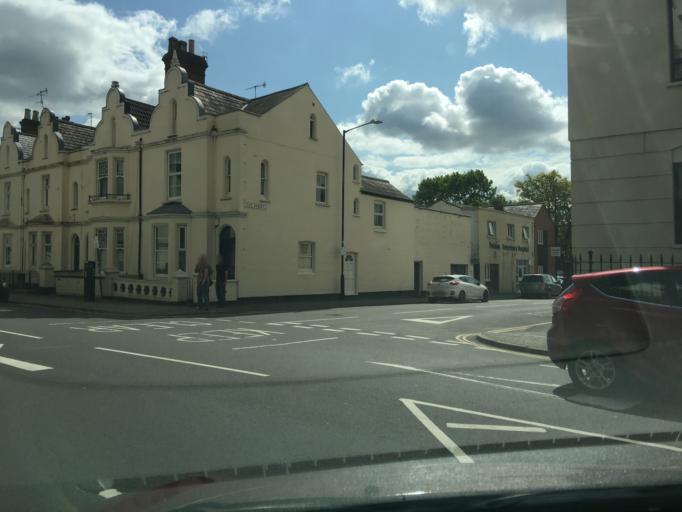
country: GB
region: England
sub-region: Warwickshire
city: Royal Leamington Spa
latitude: 52.2938
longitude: -1.5351
